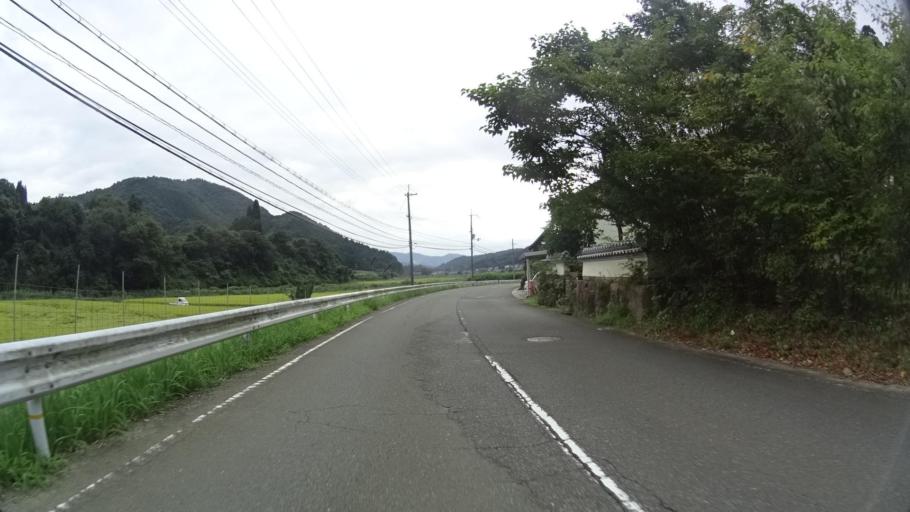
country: JP
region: Kyoto
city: Miyazu
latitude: 35.4213
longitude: 135.1567
